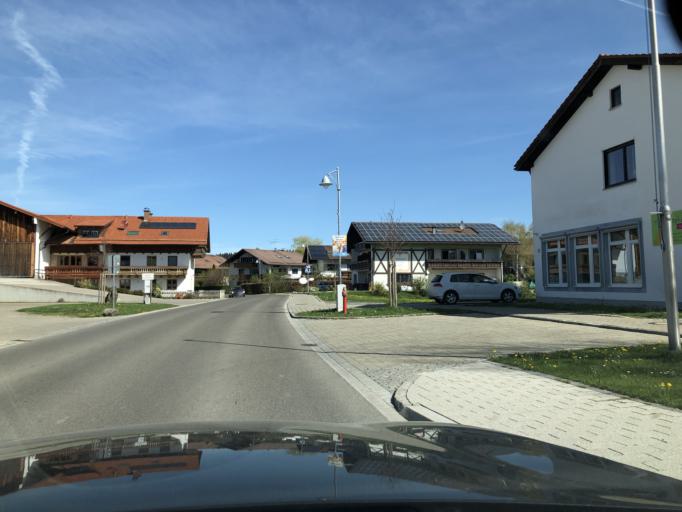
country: DE
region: Bavaria
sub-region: Swabia
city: Hopferau
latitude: 47.6102
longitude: 10.6376
